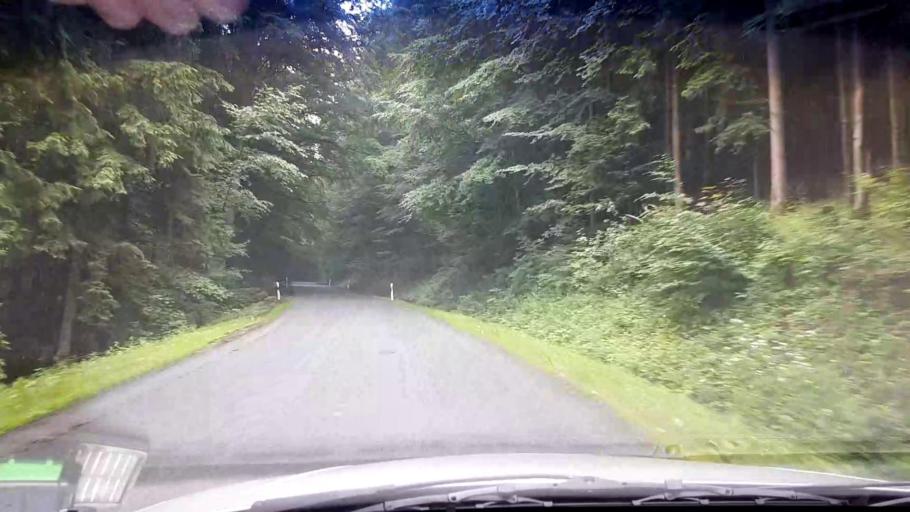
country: DE
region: Bavaria
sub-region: Upper Franconia
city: Wattendorf
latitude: 50.0597
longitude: 11.0887
